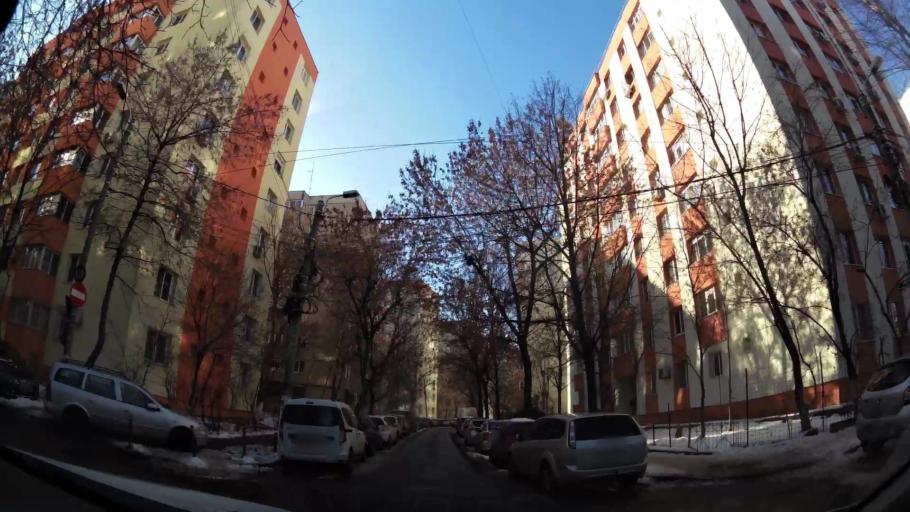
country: RO
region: Bucuresti
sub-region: Municipiul Bucuresti
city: Bucharest
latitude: 44.4612
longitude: 26.1286
